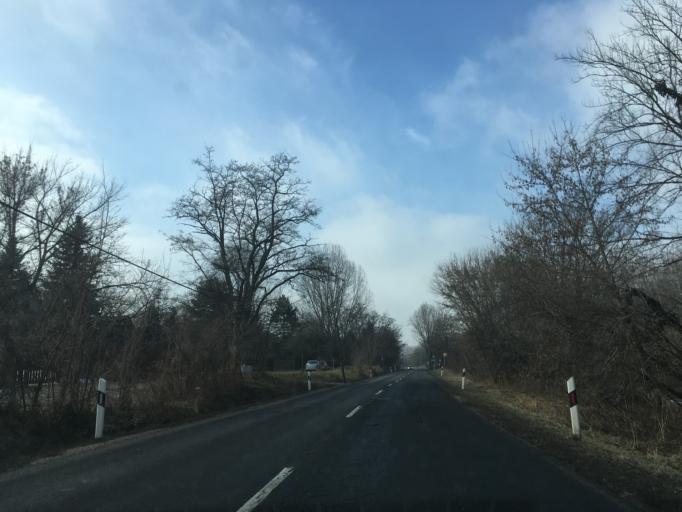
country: HU
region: Komarom-Esztergom
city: Esztergom
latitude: 47.8145
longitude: 18.7949
